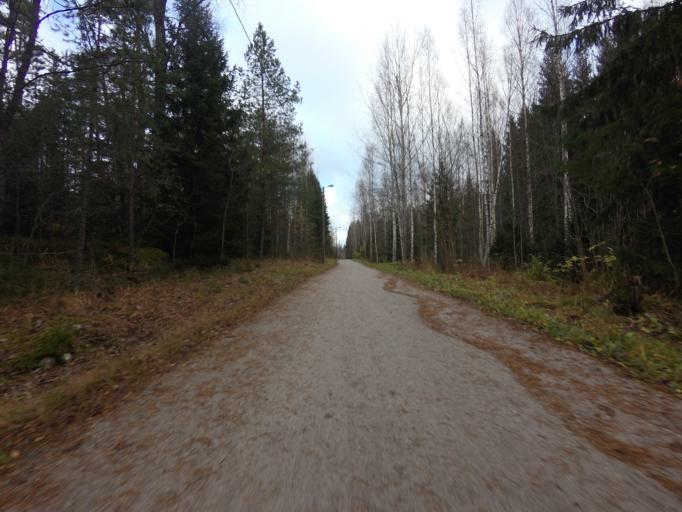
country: FI
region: Uusimaa
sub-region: Helsinki
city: Kauniainen
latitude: 60.1940
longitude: 24.6983
